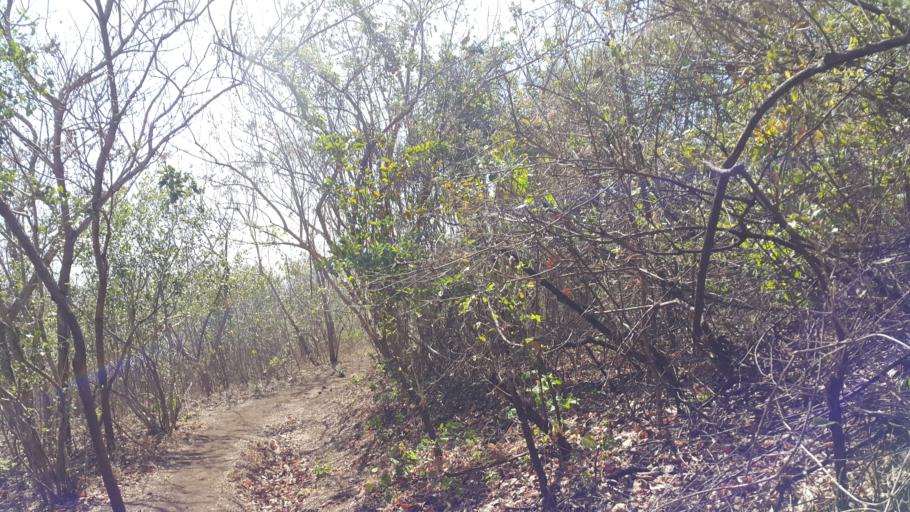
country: NI
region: Leon
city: La Paz Centro
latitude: 12.4590
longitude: -86.6718
